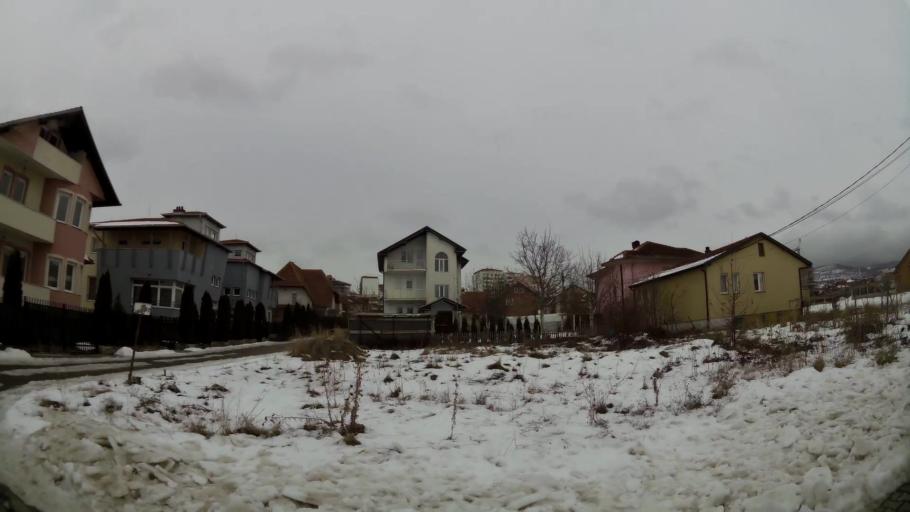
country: XK
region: Pristina
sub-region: Komuna e Prishtines
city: Pristina
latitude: 42.6443
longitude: 21.1799
